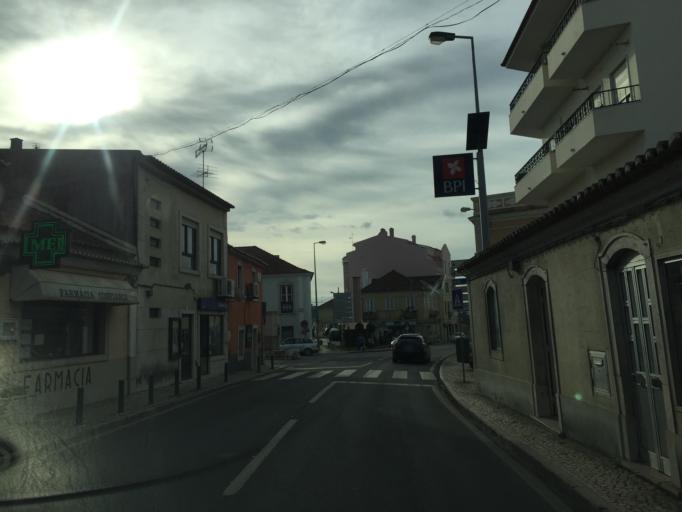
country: PT
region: Lisbon
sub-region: Sintra
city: Pero Pinheiro
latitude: 38.8568
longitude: -9.3258
